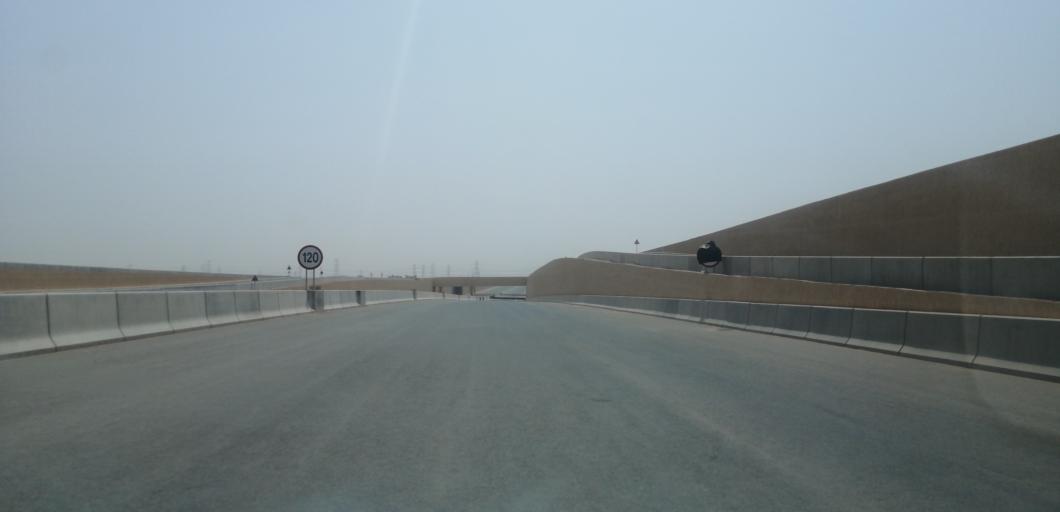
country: KW
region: Muhafazat al Jahra'
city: Al Jahra'
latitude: 29.4516
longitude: 47.6011
